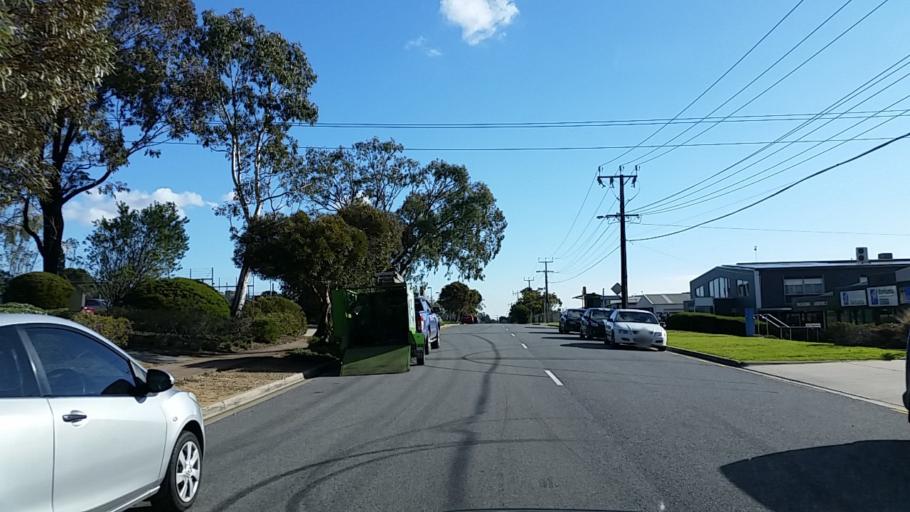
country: AU
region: South Australia
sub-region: Tea Tree Gully
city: Modbury
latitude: -34.8475
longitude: 138.6753
